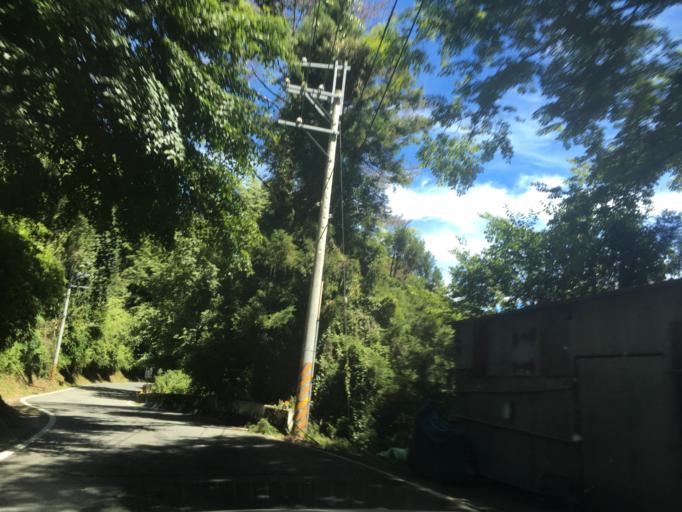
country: TW
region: Taiwan
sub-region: Nantou
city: Puli
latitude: 24.2251
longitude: 121.2570
